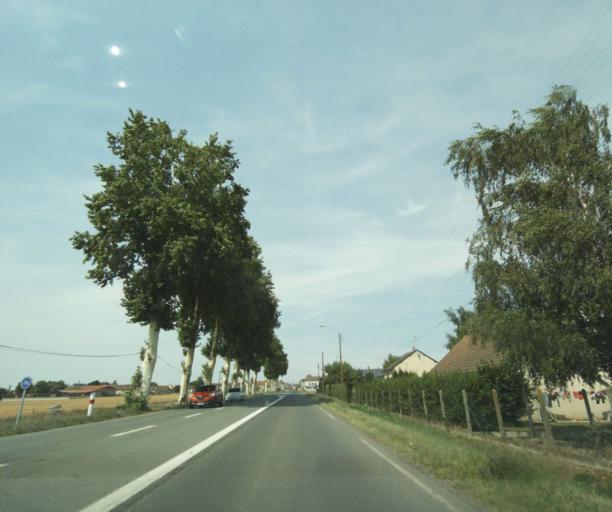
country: FR
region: Centre
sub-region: Departement d'Indre-et-Loire
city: La Celle-Saint-Avant
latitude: 47.0171
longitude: 0.6029
